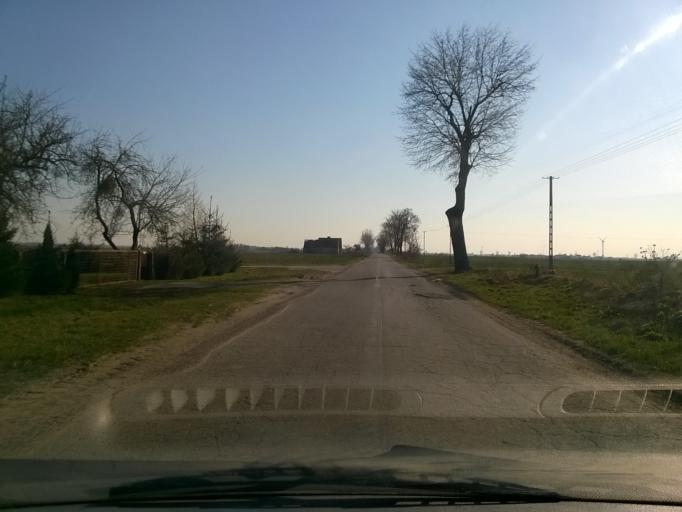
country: PL
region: Greater Poland Voivodeship
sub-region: Powiat wagrowiecki
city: Golancz
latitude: 52.9796
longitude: 17.3380
